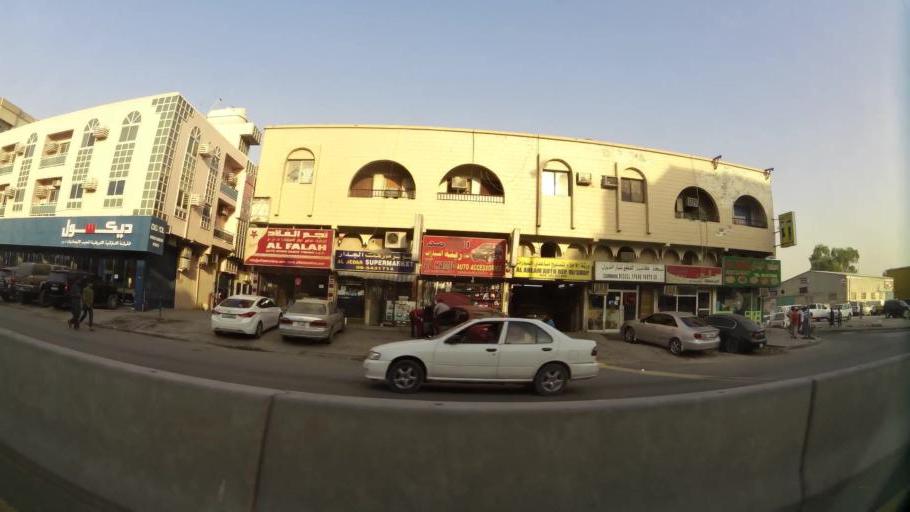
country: AE
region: Ash Shariqah
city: Sharjah
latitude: 25.3280
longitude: 55.4078
